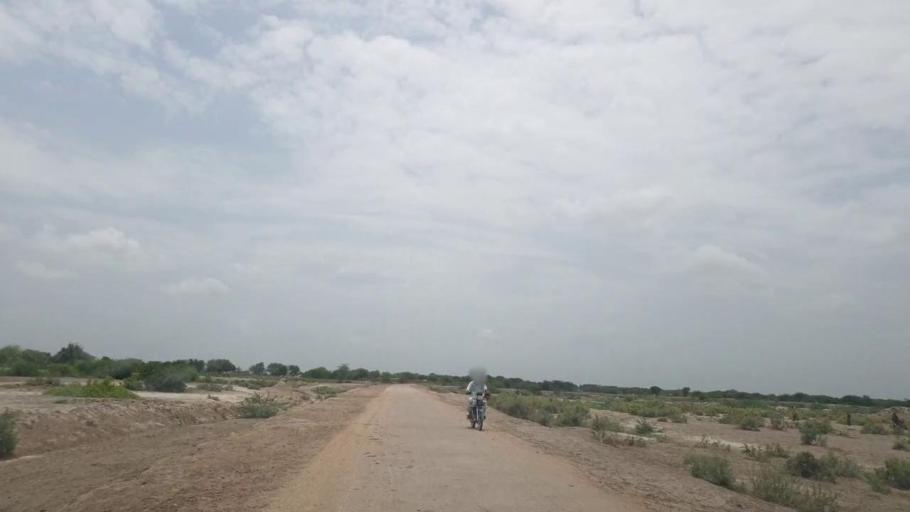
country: PK
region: Sindh
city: Naukot
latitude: 24.9350
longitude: 69.1835
